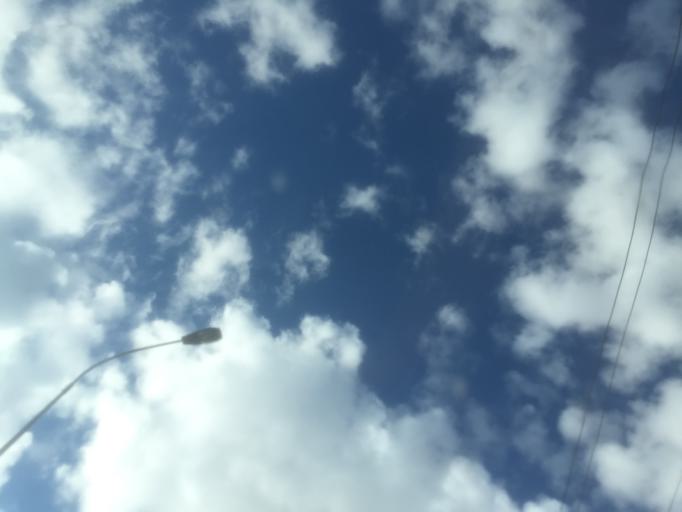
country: KZ
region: Astana Qalasy
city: Astana
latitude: 51.1919
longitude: 71.3998
